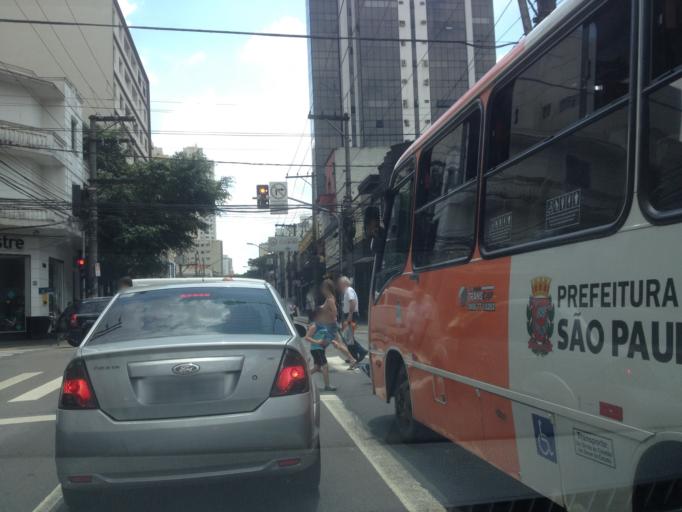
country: BR
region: Sao Paulo
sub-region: Sao Paulo
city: Sao Paulo
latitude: -23.5631
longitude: -46.6867
